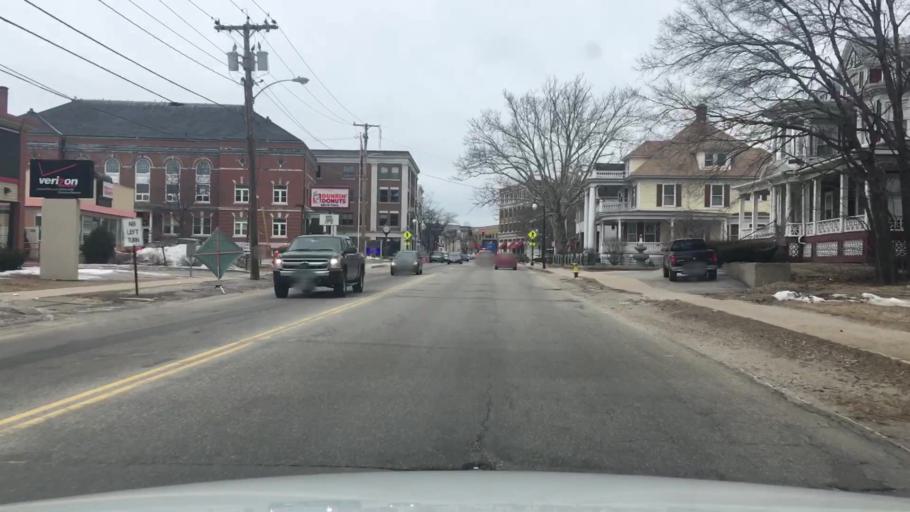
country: US
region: Maine
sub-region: York County
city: Sanford (historical)
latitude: 43.4374
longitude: -70.7740
